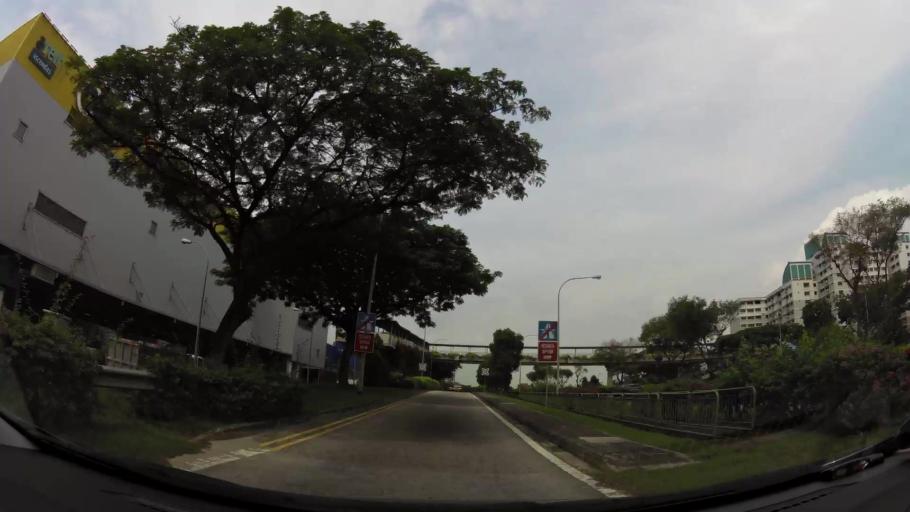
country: MY
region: Johor
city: Kampung Pasir Gudang Baru
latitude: 1.3743
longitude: 103.9345
